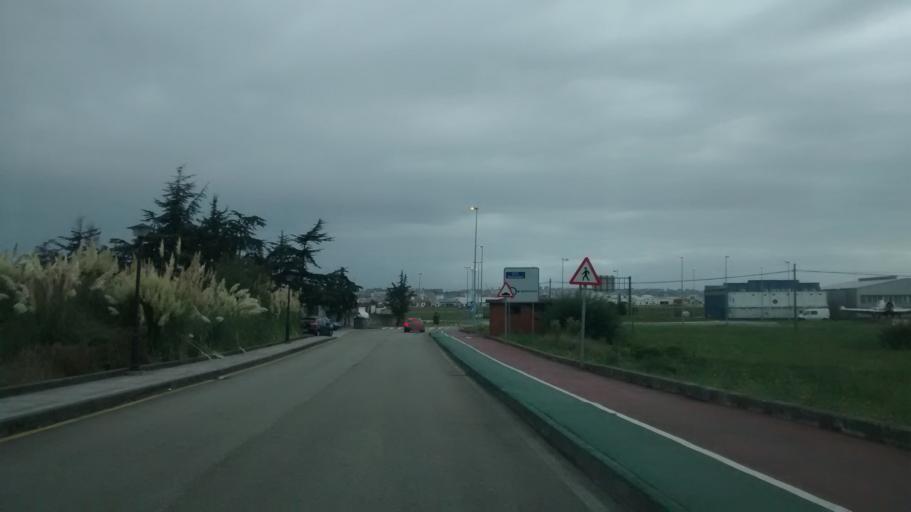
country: ES
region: Cantabria
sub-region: Provincia de Cantabria
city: El Astillero
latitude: 43.4226
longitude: -3.8287
